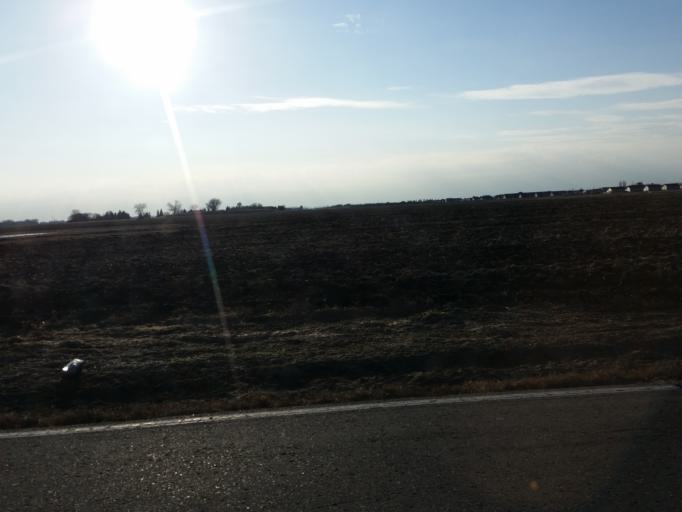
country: US
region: North Dakota
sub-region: Grand Forks County
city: Grand Forks
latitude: 47.8624
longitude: -97.0291
